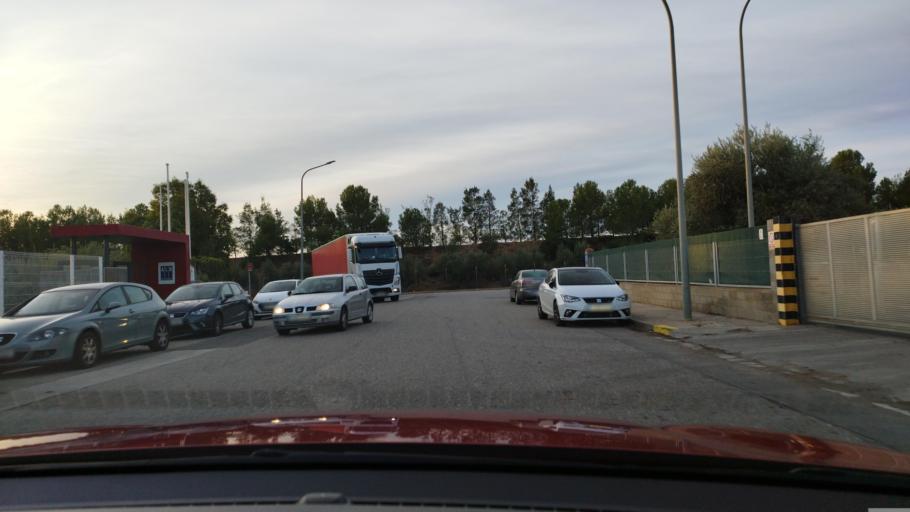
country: ES
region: Catalonia
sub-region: Provincia de Tarragona
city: la Bisbal del Penedes
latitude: 41.2697
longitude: 1.5167
